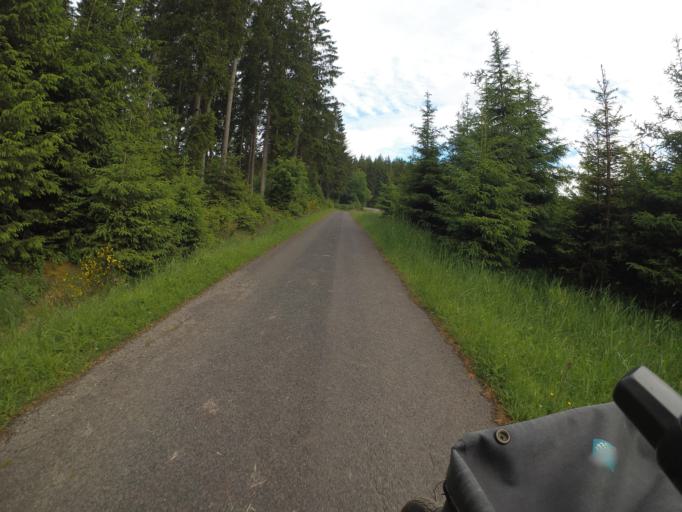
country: DE
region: Rheinland-Pfalz
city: Scheid
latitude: 50.3866
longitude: 6.3927
